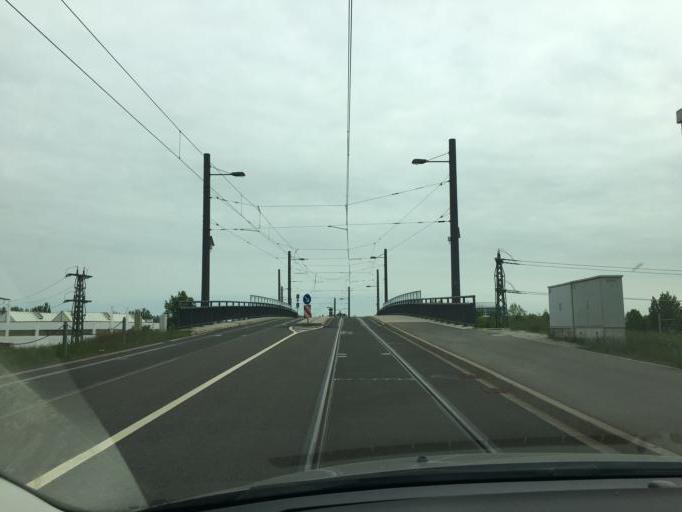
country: DE
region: Saxony
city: Taucha
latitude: 51.3664
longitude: 12.4503
